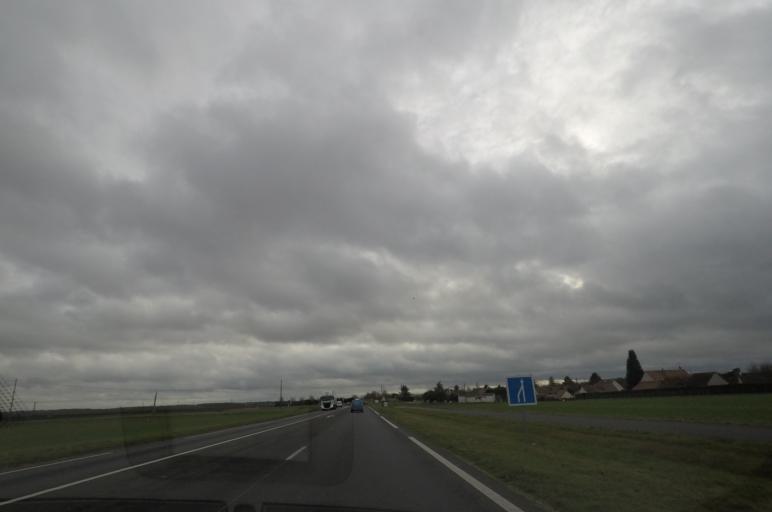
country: FR
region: Centre
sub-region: Departement du Loir-et-Cher
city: Saint-Sulpice-de-Pommeray
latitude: 47.6609
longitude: 1.2615
